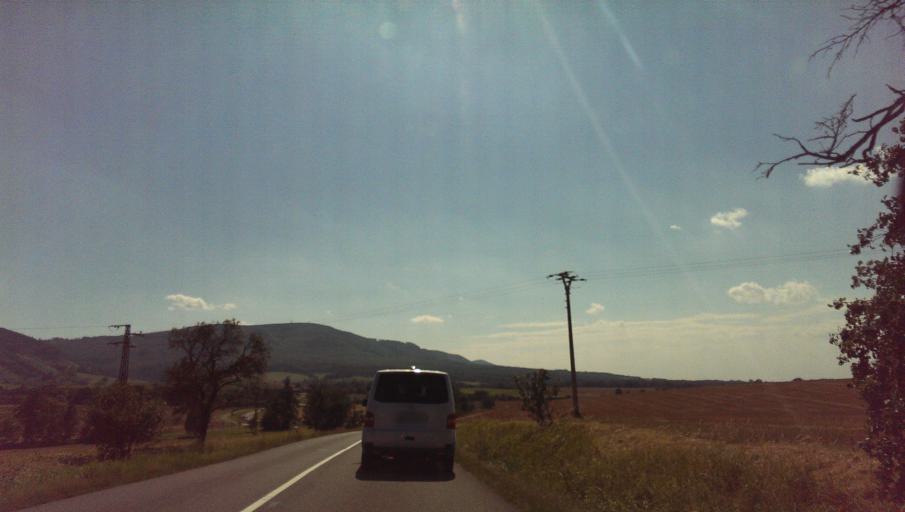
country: CZ
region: Zlin
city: Kelc
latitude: 49.4391
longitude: 17.8057
